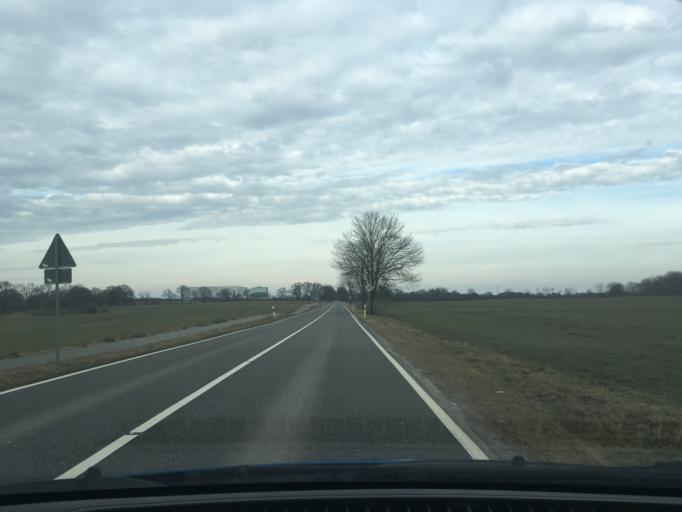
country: DE
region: Mecklenburg-Vorpommern
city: Zarrentin
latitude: 53.5334
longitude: 10.8985
